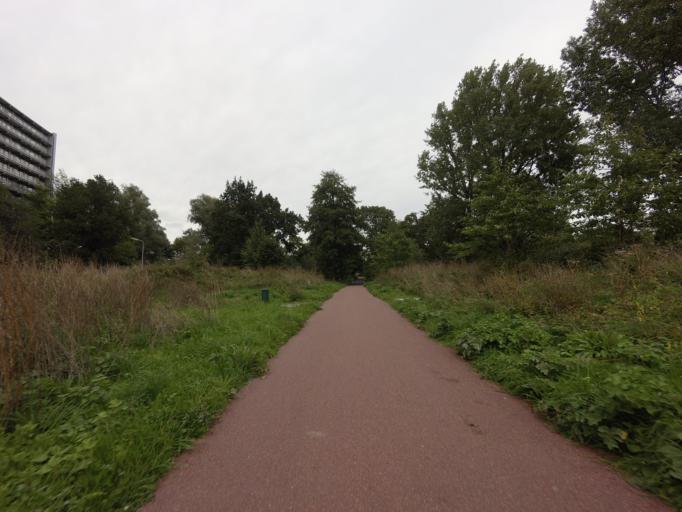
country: NL
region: Friesland
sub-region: Gemeente Leeuwarden
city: Bilgaard
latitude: 53.2169
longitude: 5.7916
